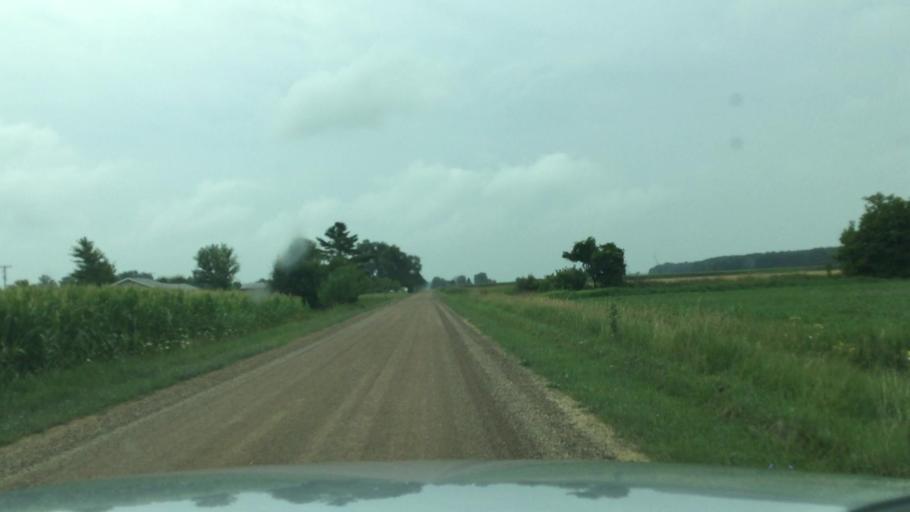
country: US
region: Michigan
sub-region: Shiawassee County
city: New Haven
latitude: 43.1155
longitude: -84.2320
